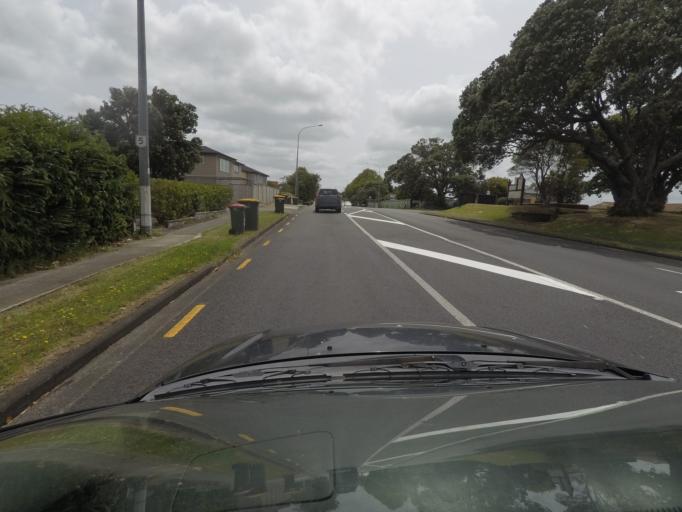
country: NZ
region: Auckland
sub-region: Auckland
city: Pakuranga
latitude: -36.8986
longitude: 174.9197
